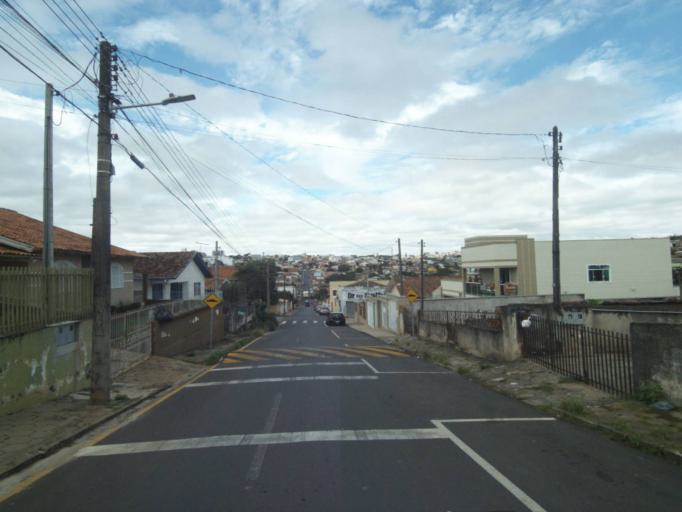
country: BR
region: Parana
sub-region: Telemaco Borba
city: Telemaco Borba
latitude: -24.3231
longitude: -50.6223
